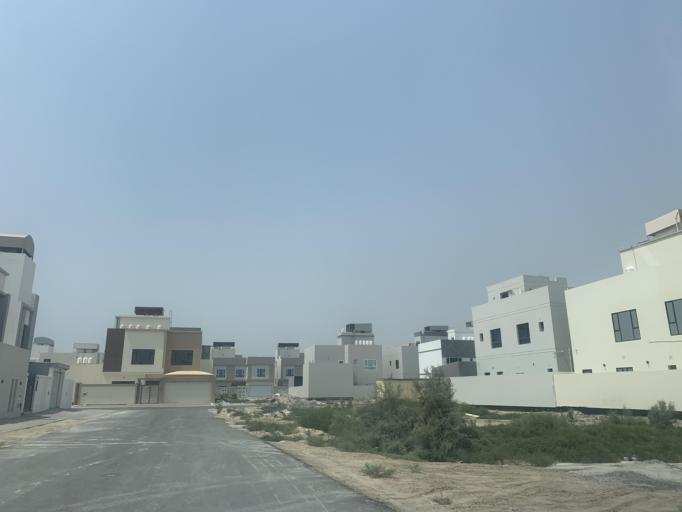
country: BH
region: Central Governorate
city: Madinat Hamad
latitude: 26.1282
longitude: 50.4682
